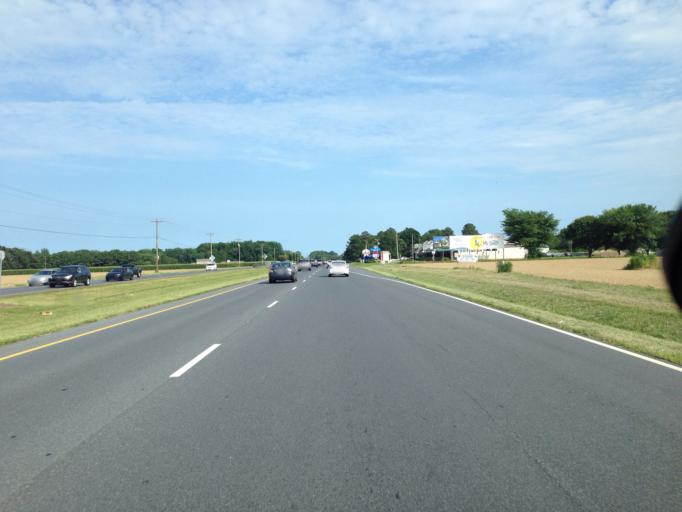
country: US
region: Delaware
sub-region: Sussex County
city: Lewes
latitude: 38.7671
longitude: -75.2139
